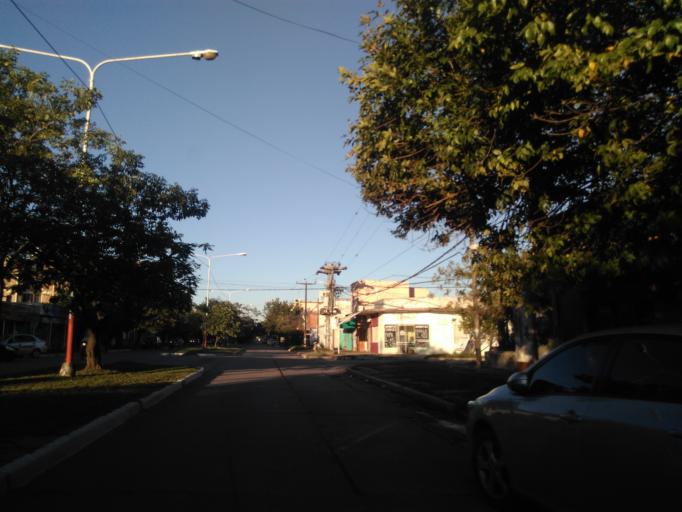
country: AR
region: Chaco
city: Resistencia
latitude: -27.4548
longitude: -58.9994
